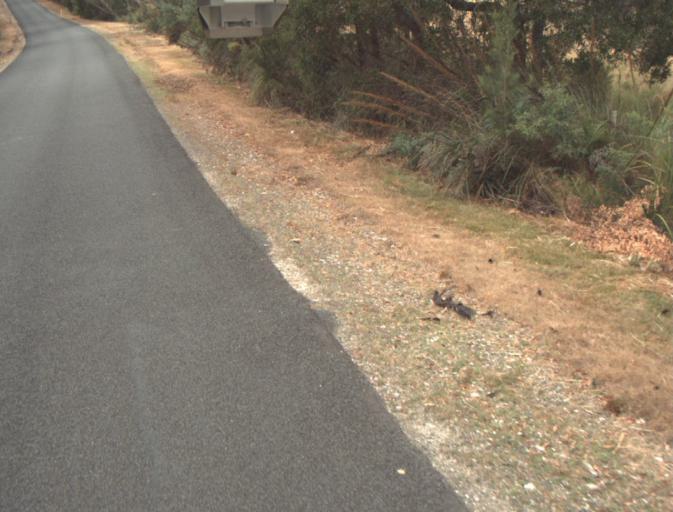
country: AU
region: Tasmania
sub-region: Launceston
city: Mayfield
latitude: -41.2174
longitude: 147.0510
